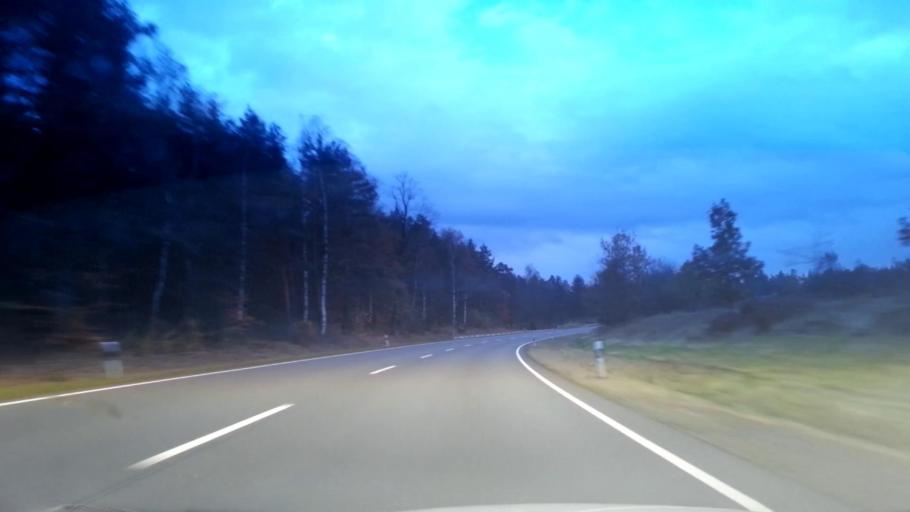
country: DE
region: Bavaria
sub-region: Upper Palatinate
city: Pechbrunn
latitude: 49.9589
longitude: 12.1921
